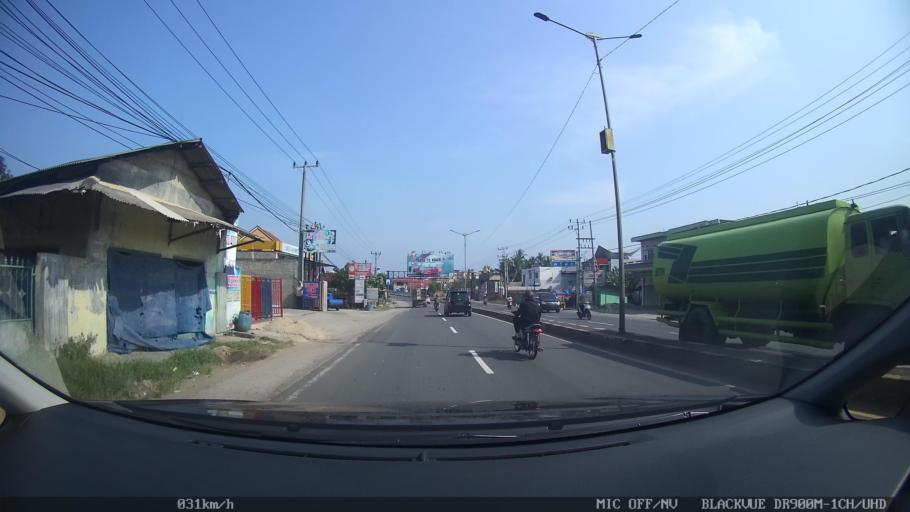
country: ID
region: Lampung
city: Natar
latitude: -5.2511
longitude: 105.1819
